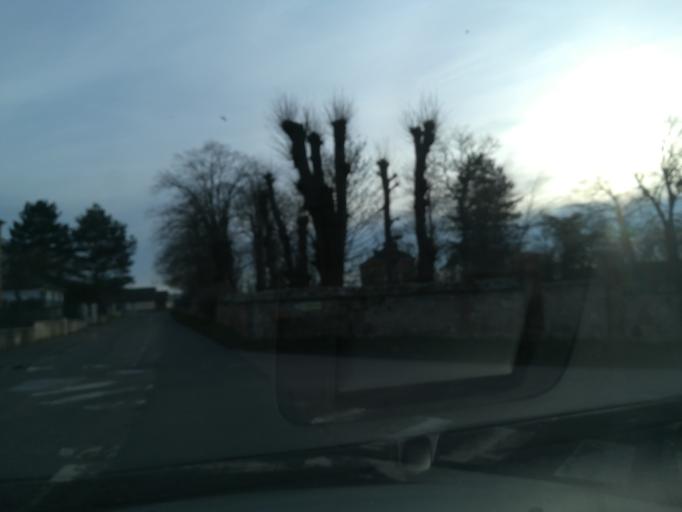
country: FR
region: Haute-Normandie
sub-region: Departement de la Seine-Maritime
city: Saint-Martin-de-Boscherville
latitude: 49.4413
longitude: 0.9633
